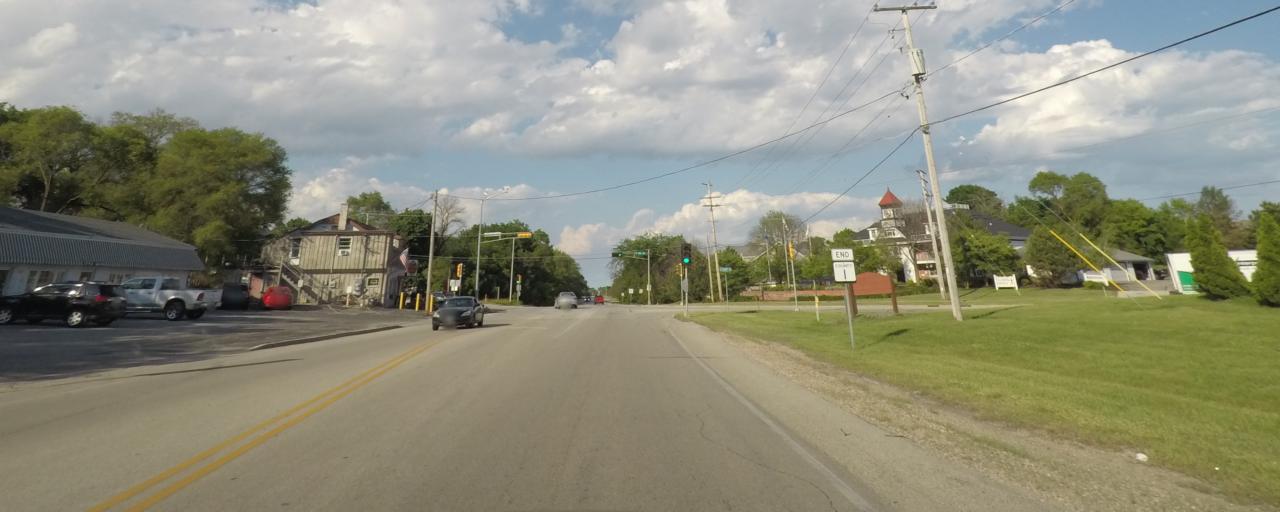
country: US
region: Wisconsin
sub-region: Milwaukee County
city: Hales Corners
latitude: 42.9634
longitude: -88.0699
